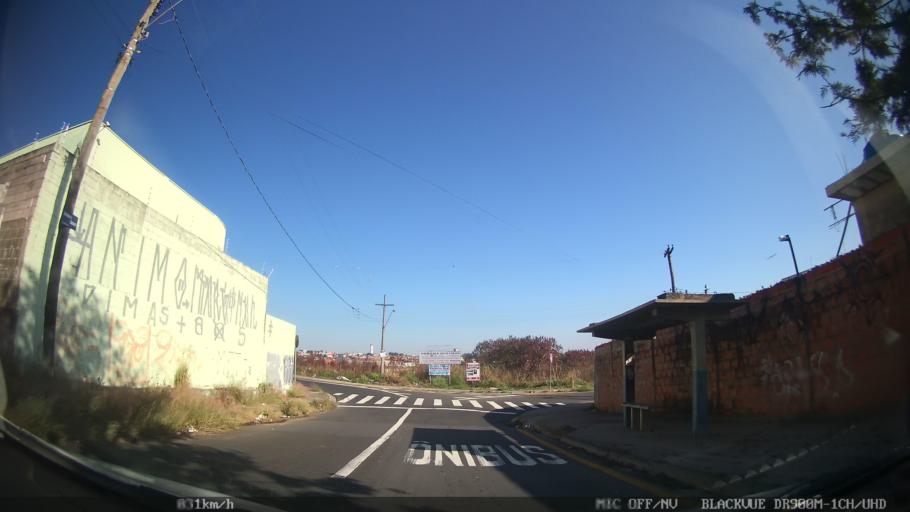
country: BR
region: Sao Paulo
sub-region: Campinas
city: Campinas
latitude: -22.9855
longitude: -47.1102
